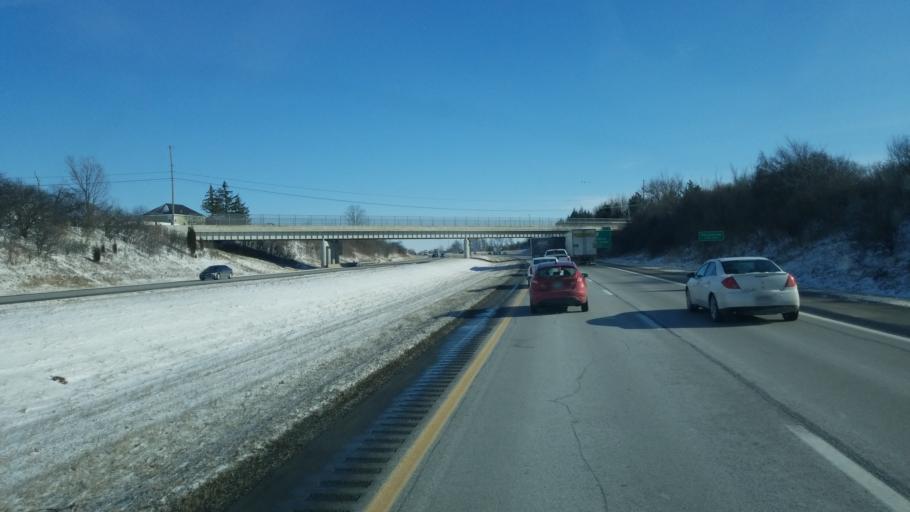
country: US
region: Ohio
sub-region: Lucas County
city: Maumee
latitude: 41.5383
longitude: -83.6765
